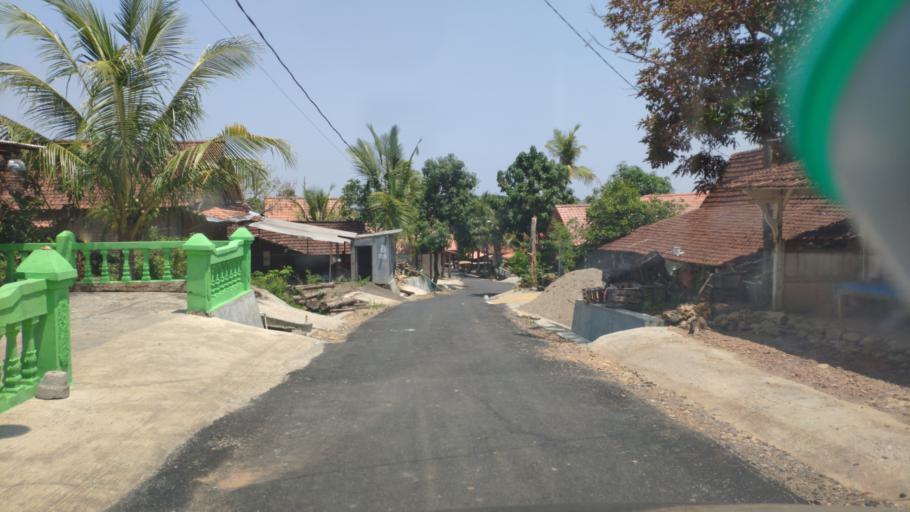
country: ID
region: Central Java
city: Ngapus
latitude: -6.9309
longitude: 111.1867
